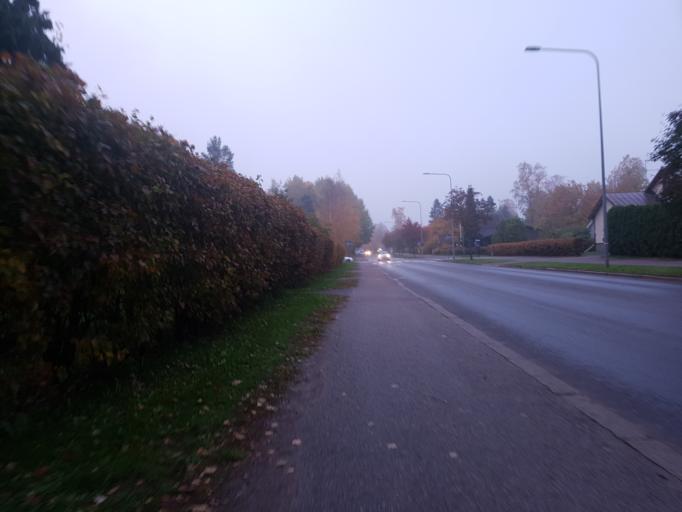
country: FI
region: Uusimaa
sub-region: Helsinki
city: Helsinki
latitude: 60.2524
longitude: 24.9191
